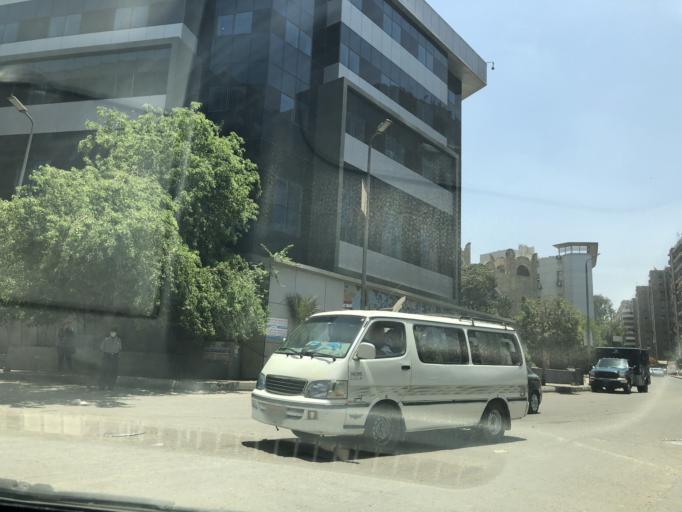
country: EG
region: Muhafazat al Qahirah
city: Cairo
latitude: 30.0626
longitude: 31.2736
